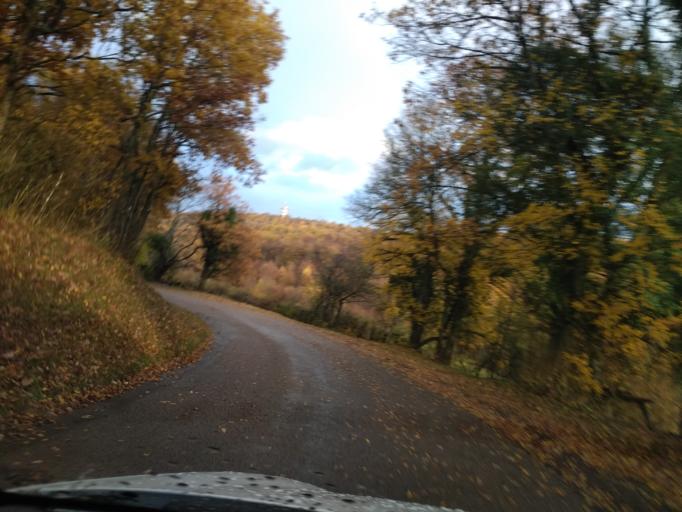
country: FR
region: Bourgogne
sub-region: Departement de Saone-et-Loire
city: Rully
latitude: 46.8803
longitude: 4.7125
